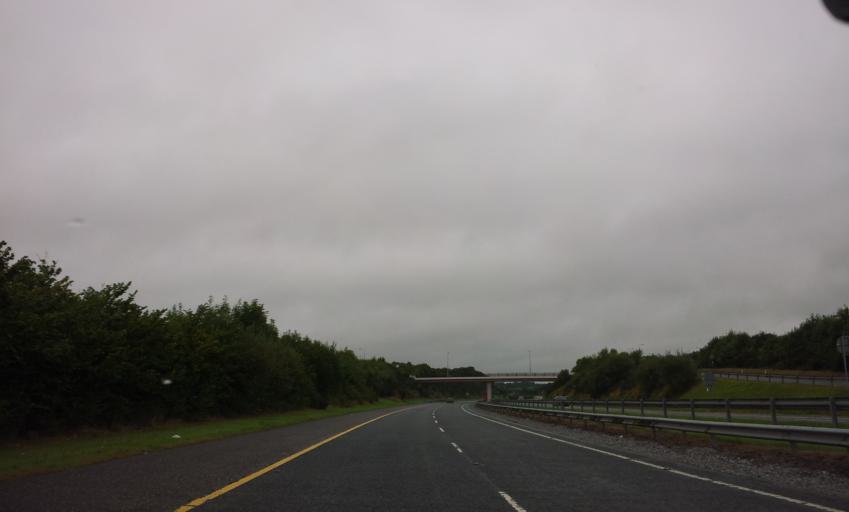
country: IE
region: Munster
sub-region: County Cork
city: Watergrasshill
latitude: 51.9529
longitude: -8.3903
